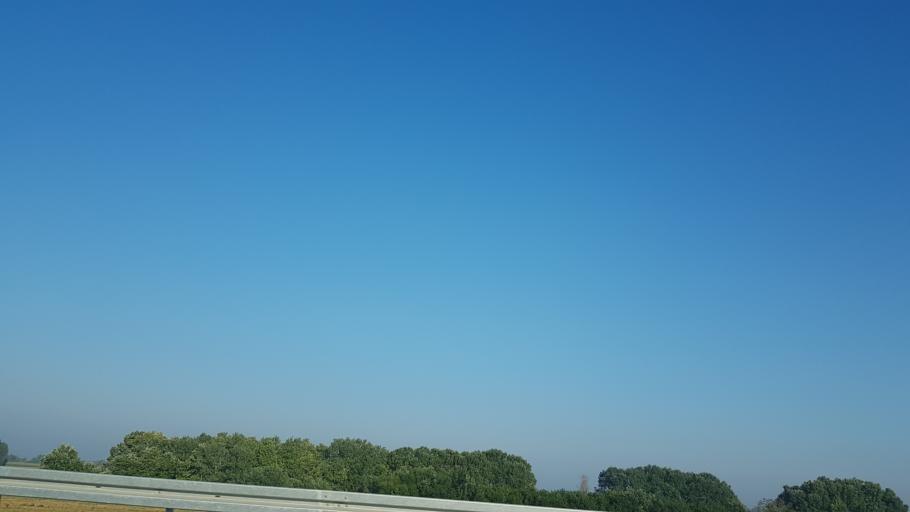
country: TR
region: Bursa
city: Karacabey
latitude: 40.1536
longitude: 28.3108
